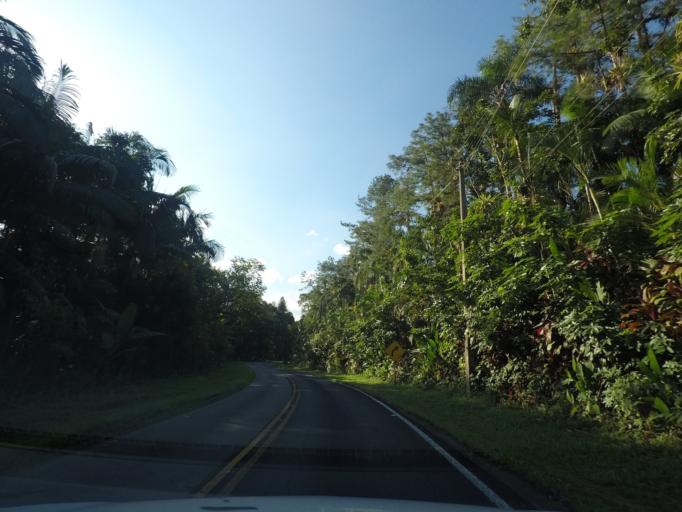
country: BR
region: Parana
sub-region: Antonina
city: Antonina
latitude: -25.4182
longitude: -48.8737
